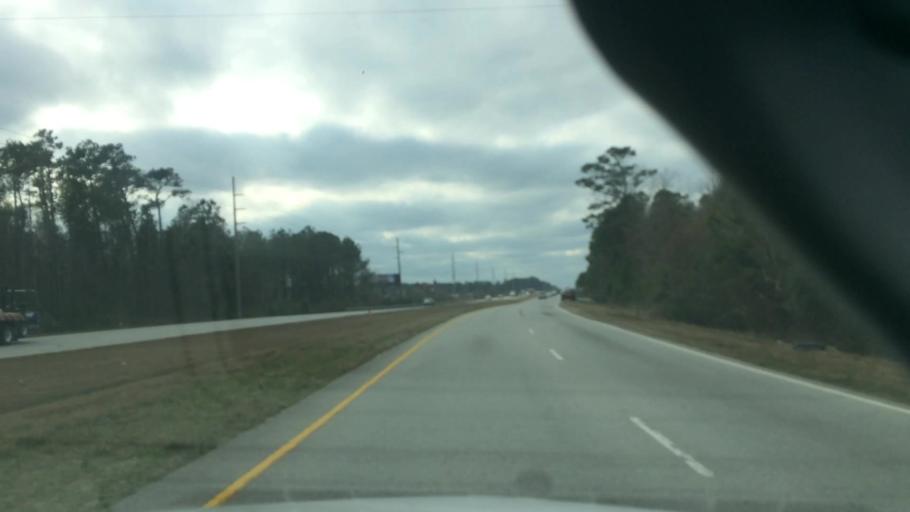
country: US
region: North Carolina
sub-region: Brunswick County
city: Shallotte
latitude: 33.9587
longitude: -78.4227
